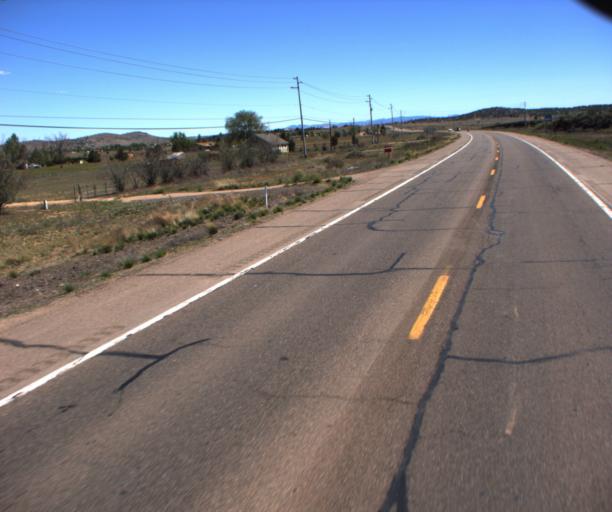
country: US
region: Arizona
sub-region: Yavapai County
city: Paulden
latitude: 34.8673
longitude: -112.4702
